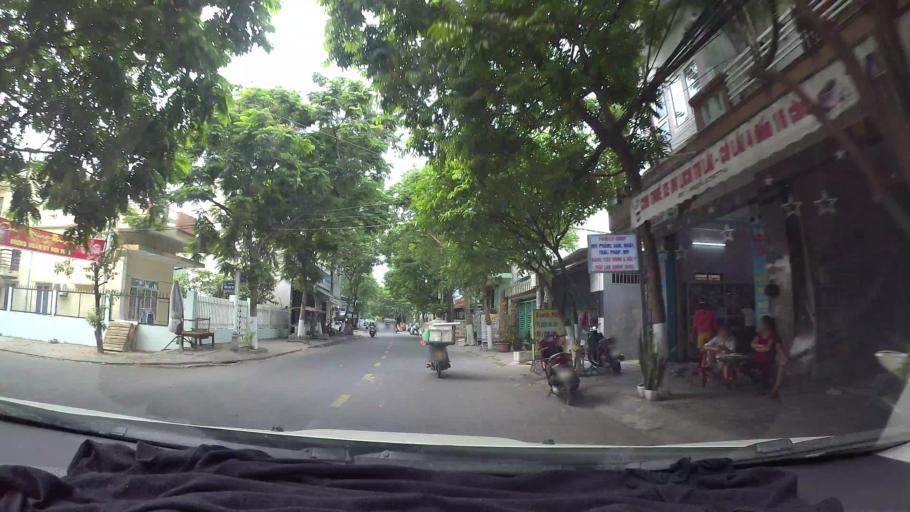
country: VN
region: Da Nang
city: Thanh Khe
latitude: 16.0578
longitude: 108.1776
